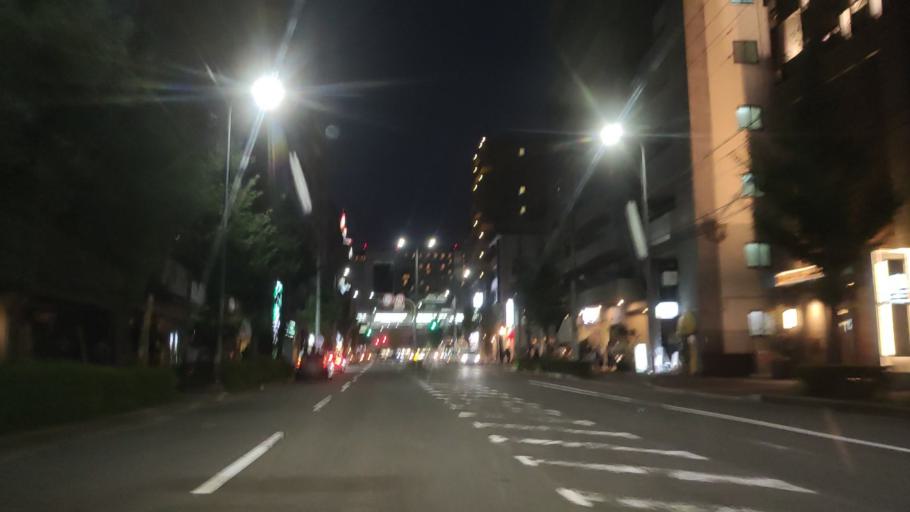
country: JP
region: Kyoto
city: Kyoto
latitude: 34.9821
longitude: 135.7598
